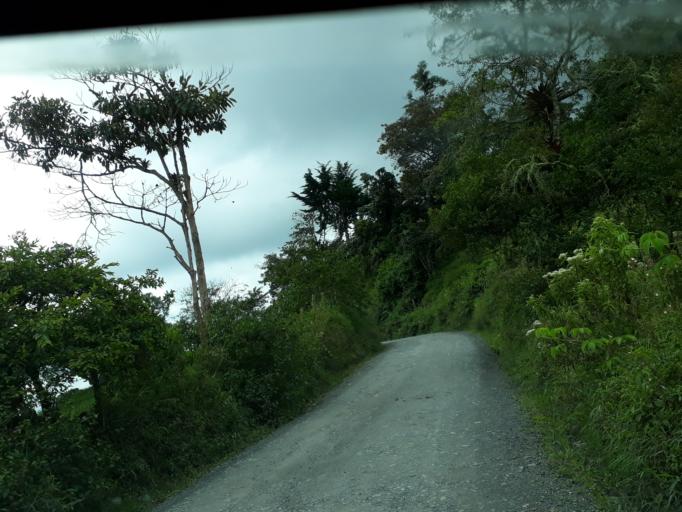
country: CO
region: Cundinamarca
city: Pacho
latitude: 5.2597
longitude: -74.1838
